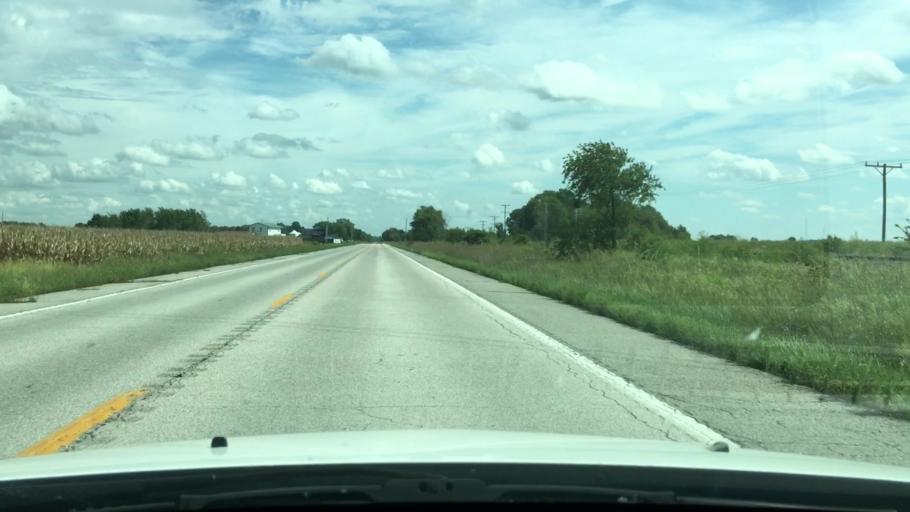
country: US
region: Missouri
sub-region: Audrain County
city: Vandalia
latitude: 39.2910
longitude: -91.5363
